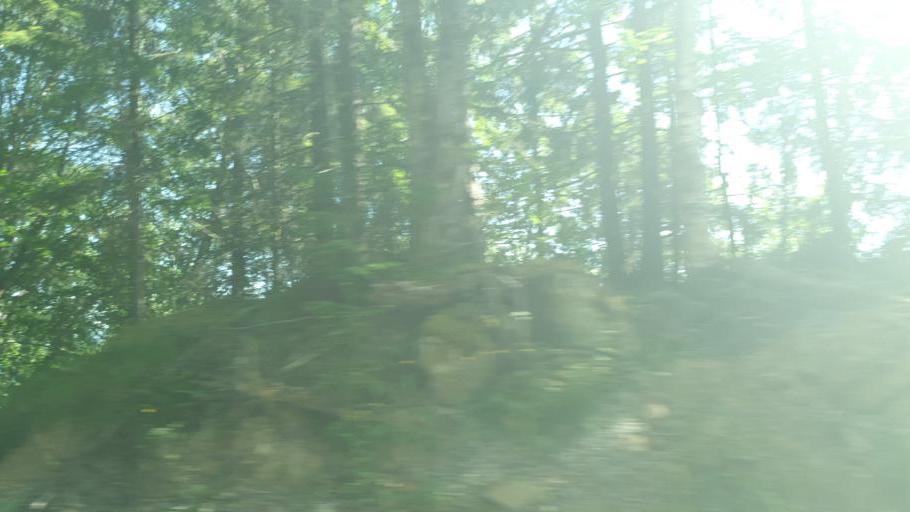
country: NO
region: Nord-Trondelag
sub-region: Frosta
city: Frosta
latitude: 63.7040
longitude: 10.7500
